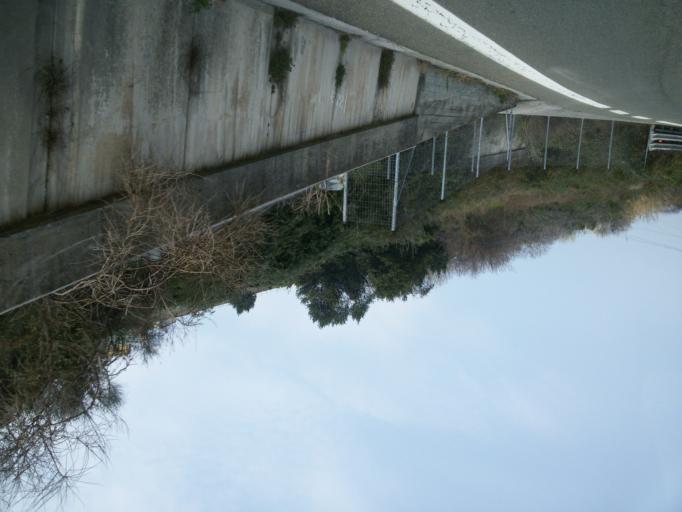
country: IT
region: Liguria
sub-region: Provincia di Genova
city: San Teodoro
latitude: 44.4221
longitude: 8.8684
